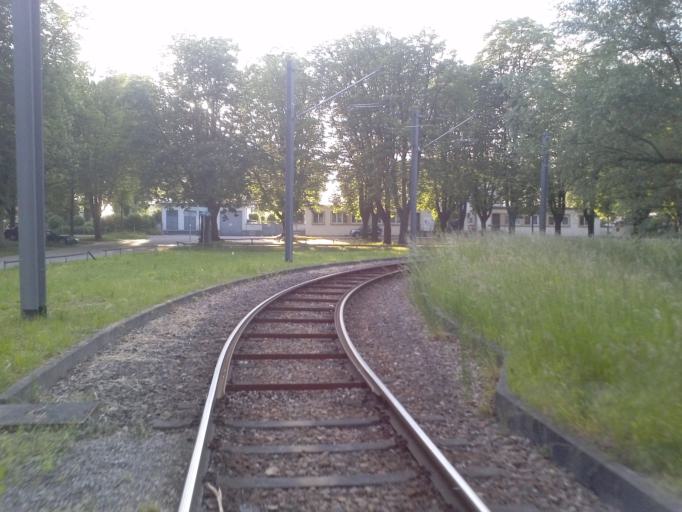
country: DE
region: Baden-Wuerttemberg
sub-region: Karlsruhe Region
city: Rheinstetten
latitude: 48.9985
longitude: 8.2953
